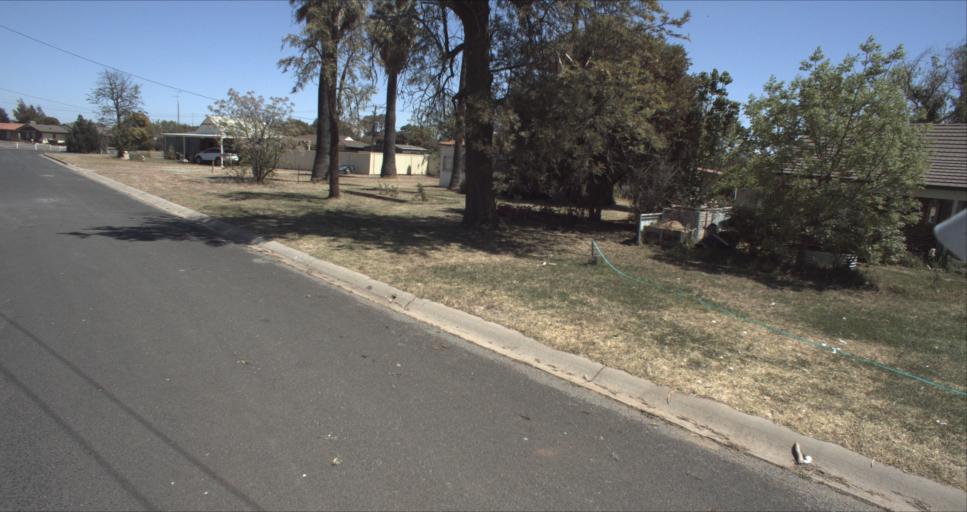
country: AU
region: New South Wales
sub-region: Leeton
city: Leeton
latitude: -34.5445
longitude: 146.4000
